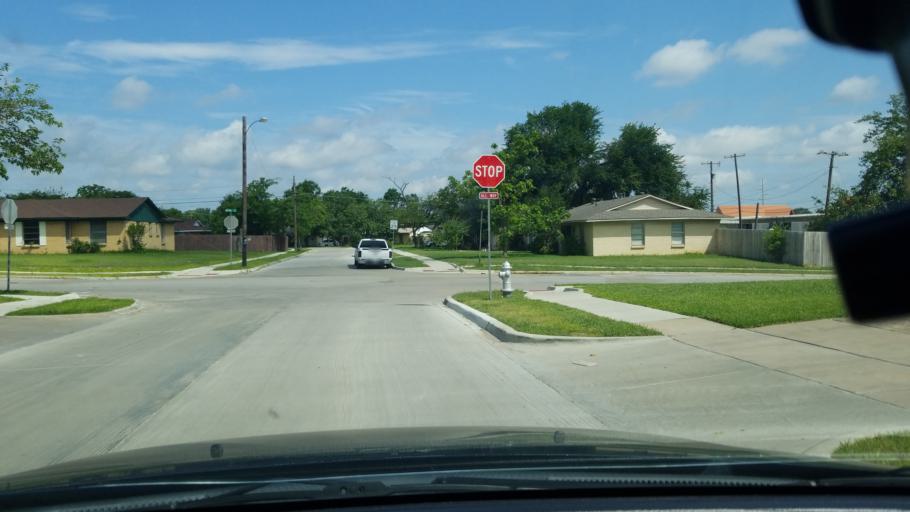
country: US
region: Texas
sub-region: Dallas County
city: Mesquite
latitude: 32.8201
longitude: -96.6472
